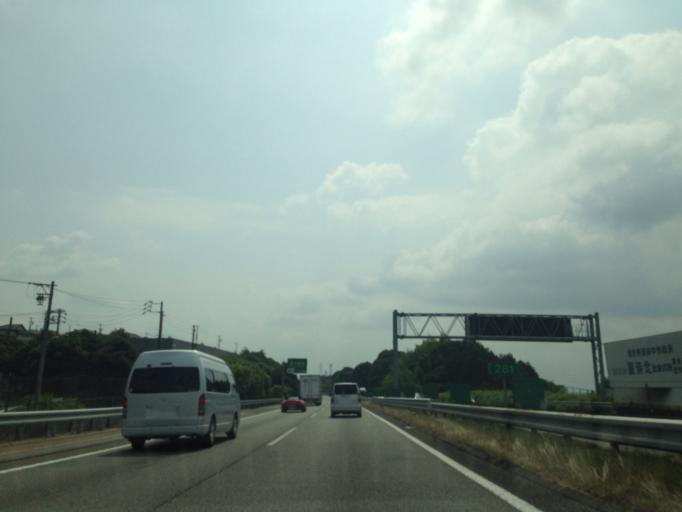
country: JP
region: Aichi
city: Gamagori
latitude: 34.8701
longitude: 137.2926
